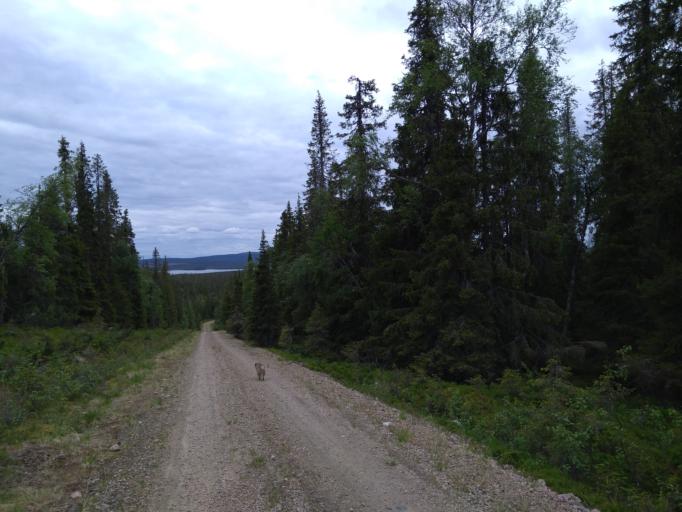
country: FI
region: Lapland
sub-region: Tunturi-Lappi
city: Muonio
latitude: 67.9664
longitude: 24.0801
